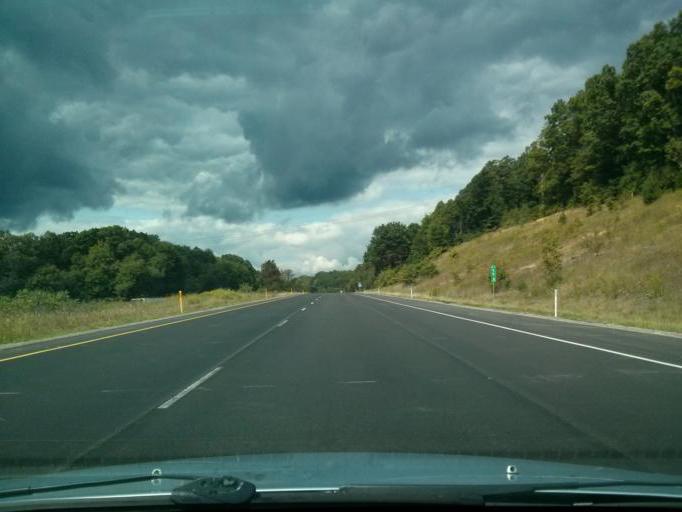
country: US
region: Pennsylvania
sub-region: Clarion County
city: Marianne
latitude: 41.1949
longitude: -79.4340
